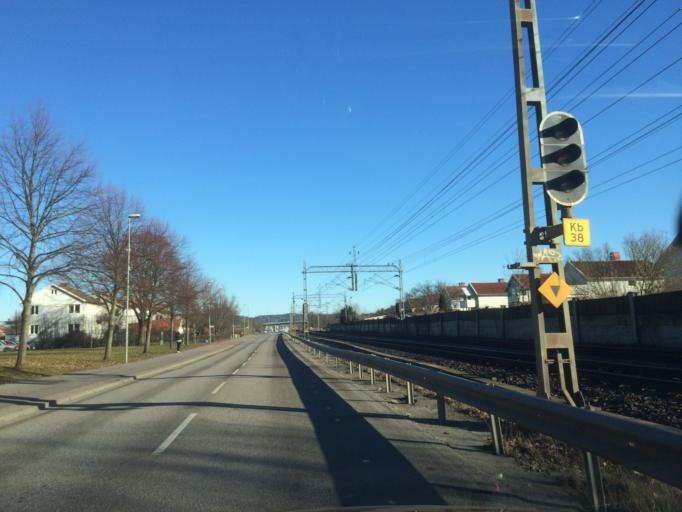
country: SE
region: Halland
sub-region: Kungsbacka Kommun
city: Kungsbacka
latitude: 57.4944
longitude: 12.0802
